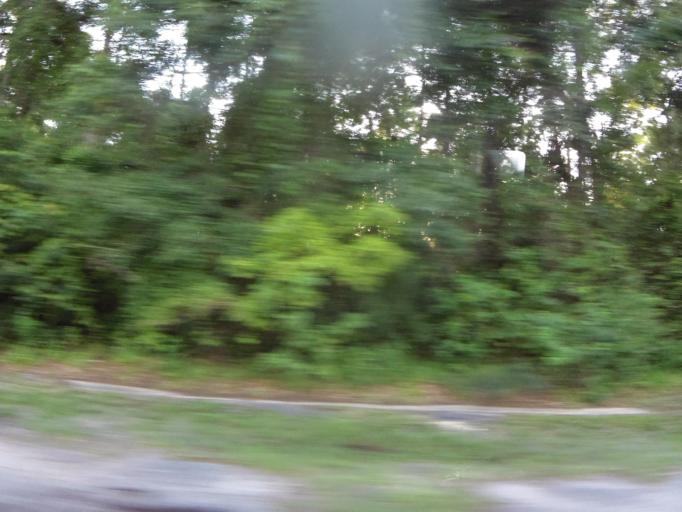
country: US
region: Florida
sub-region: Clay County
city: Orange Park
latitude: 30.2299
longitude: -81.7015
